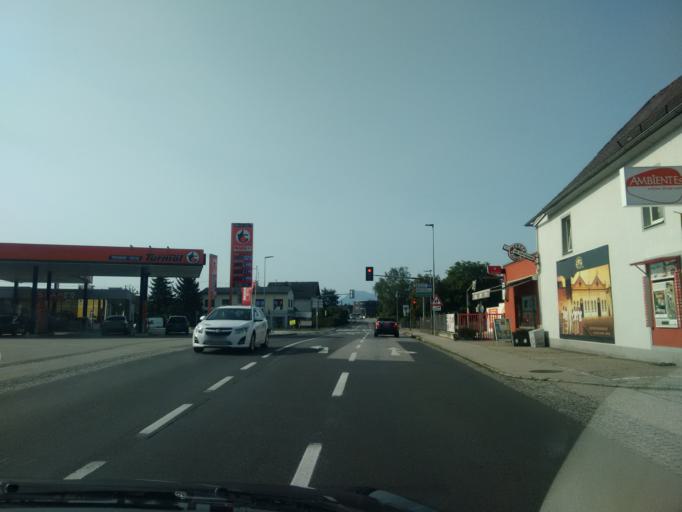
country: AT
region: Upper Austria
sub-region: Wels-Land
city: Lambach
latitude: 48.0860
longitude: 13.8737
